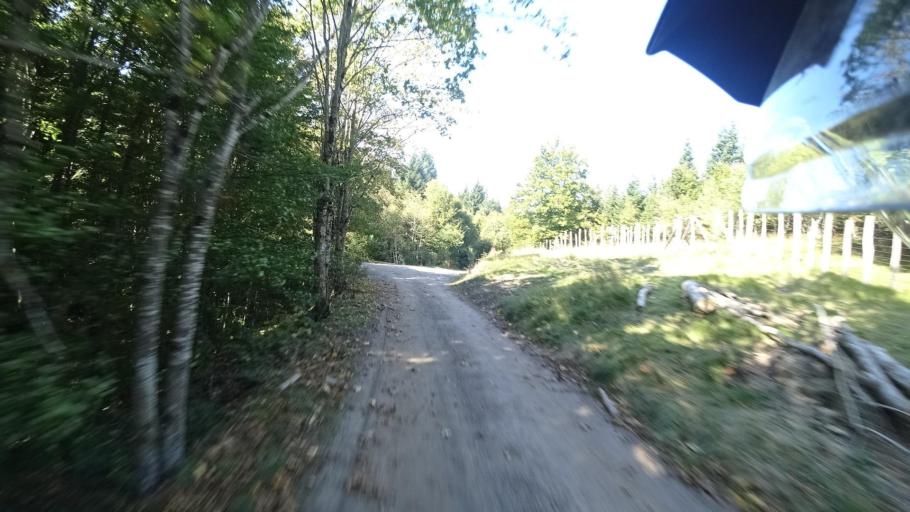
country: HR
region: Karlovacka
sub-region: Grad Ogulin
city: Ogulin
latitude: 45.2043
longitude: 15.1114
